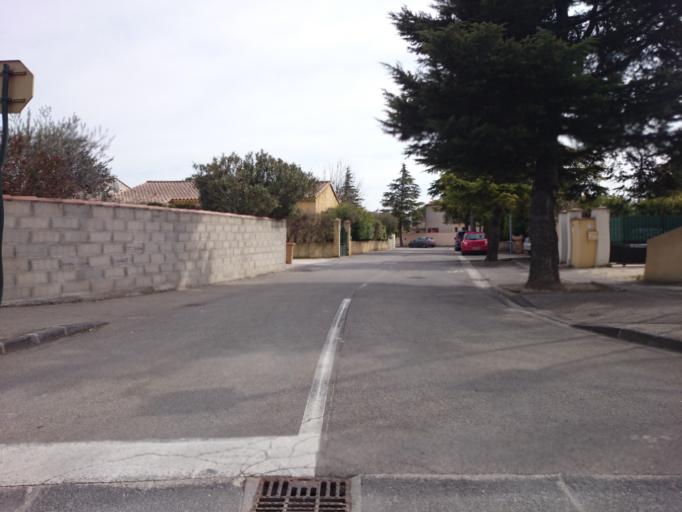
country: FR
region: Provence-Alpes-Cote d'Azur
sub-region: Departement du Vaucluse
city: Vedene
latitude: 43.9834
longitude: 4.9106
